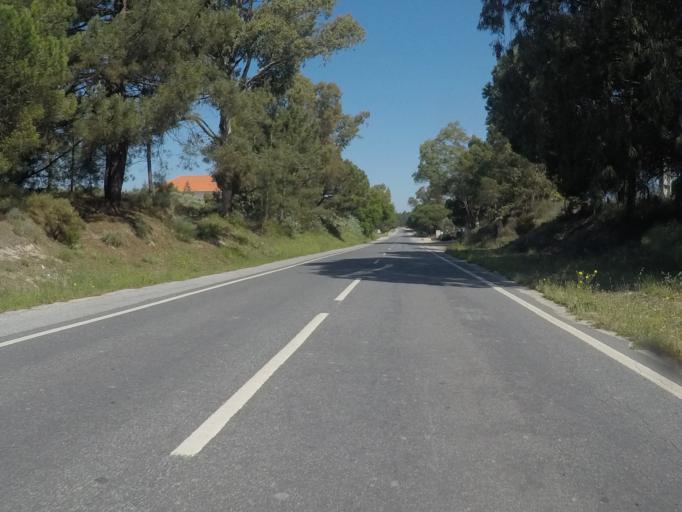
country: PT
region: Setubal
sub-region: Grandola
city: Grandola
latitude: 38.3110
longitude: -8.7433
